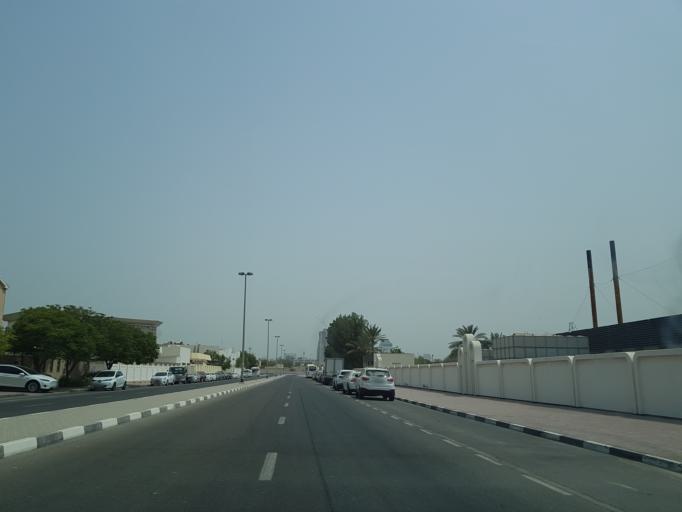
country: AE
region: Ash Shariqah
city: Sharjah
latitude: 25.2379
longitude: 55.2918
